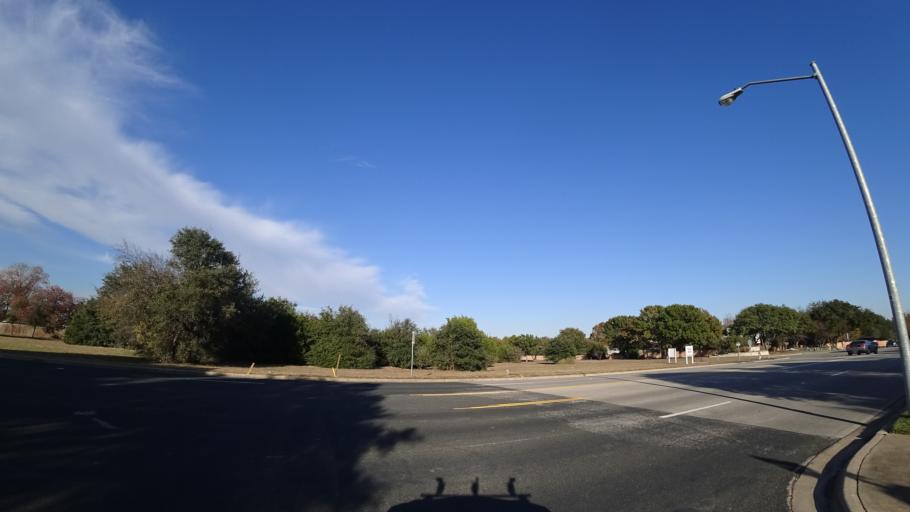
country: US
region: Texas
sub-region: Williamson County
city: Brushy Creek
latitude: 30.5061
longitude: -97.7390
